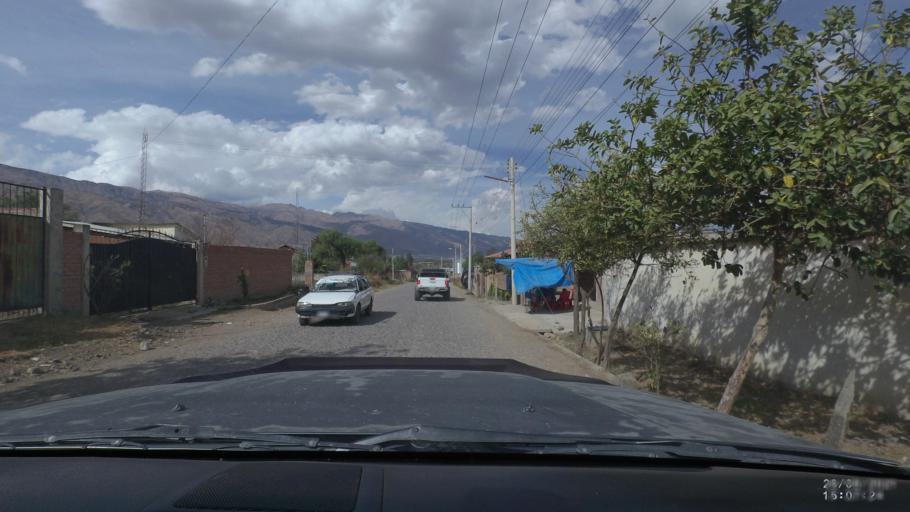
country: BO
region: Cochabamba
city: Cochabamba
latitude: -17.3371
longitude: -66.2819
